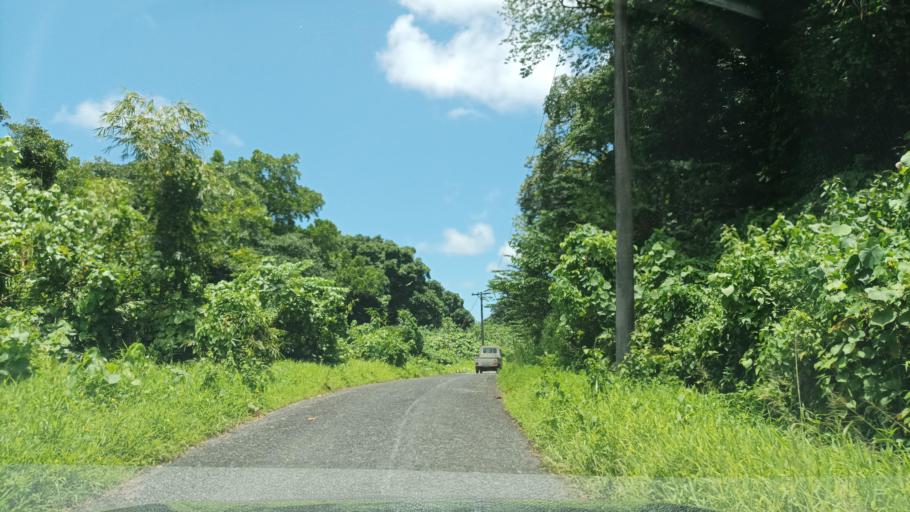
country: FM
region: Pohnpei
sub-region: Madolenihm Municipality
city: Madolenihm Municipality Government
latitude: 6.8427
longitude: 158.3105
